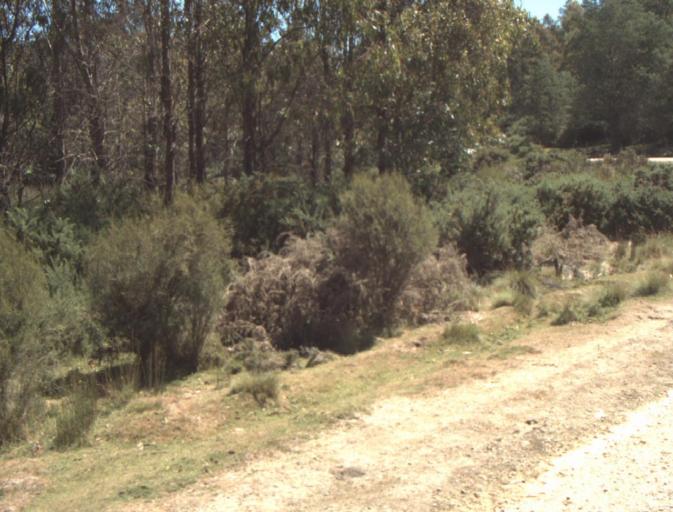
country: AU
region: Tasmania
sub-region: Dorset
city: Scottsdale
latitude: -41.3237
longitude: 147.4731
